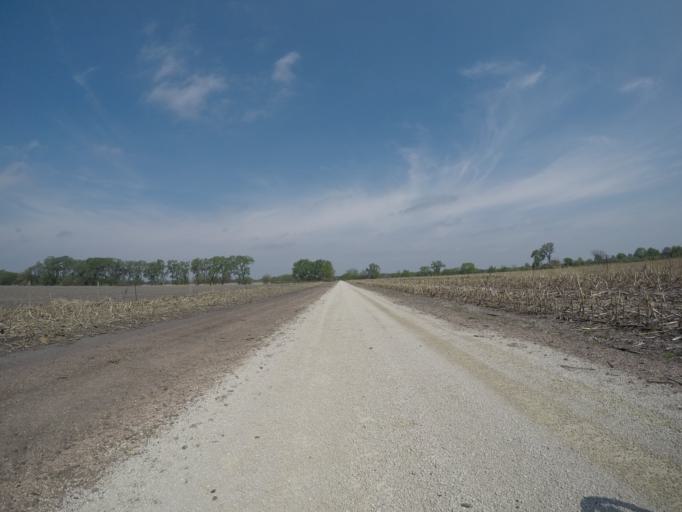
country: US
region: Nebraska
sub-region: Gage County
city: Wymore
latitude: 40.0932
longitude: -96.5999
